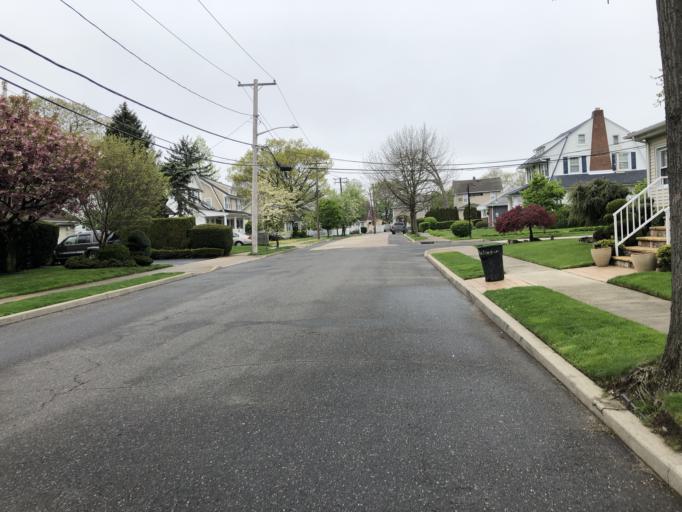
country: US
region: New York
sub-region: Nassau County
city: Lynbrook
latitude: 40.6608
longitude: -73.6640
